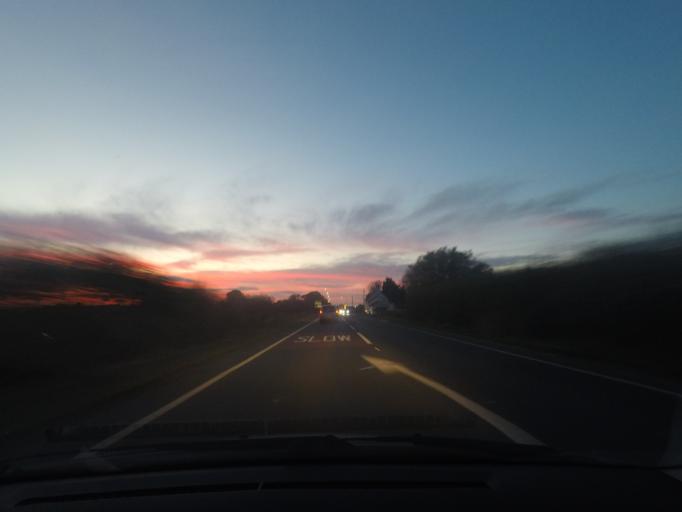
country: GB
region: England
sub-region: East Riding of Yorkshire
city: Thornton
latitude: 53.9322
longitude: -0.8337
